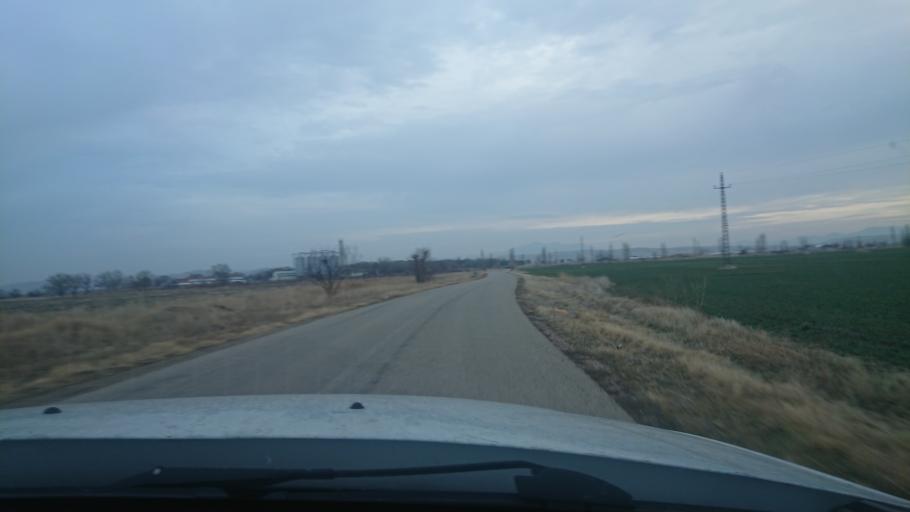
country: TR
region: Aksaray
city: Yesilova
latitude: 38.4516
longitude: 33.8350
